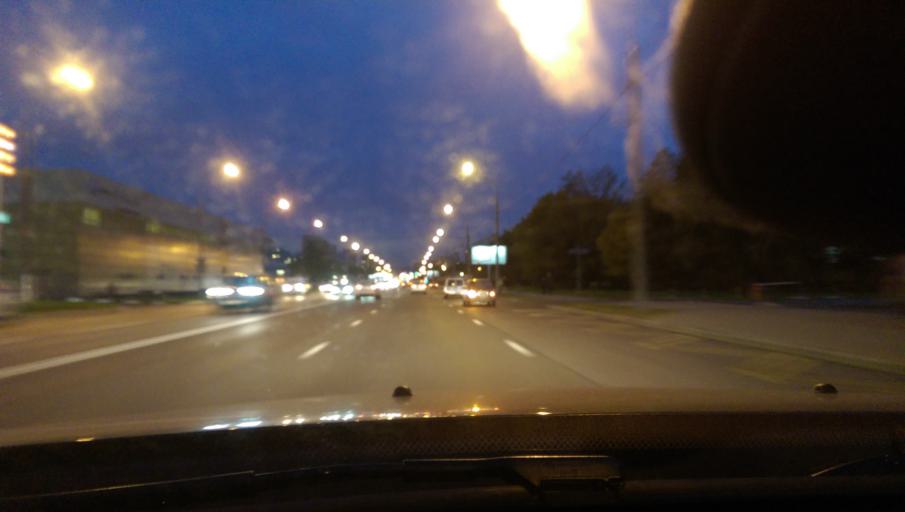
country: RU
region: Moscow
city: Vatutino
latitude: 55.8787
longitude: 37.6691
